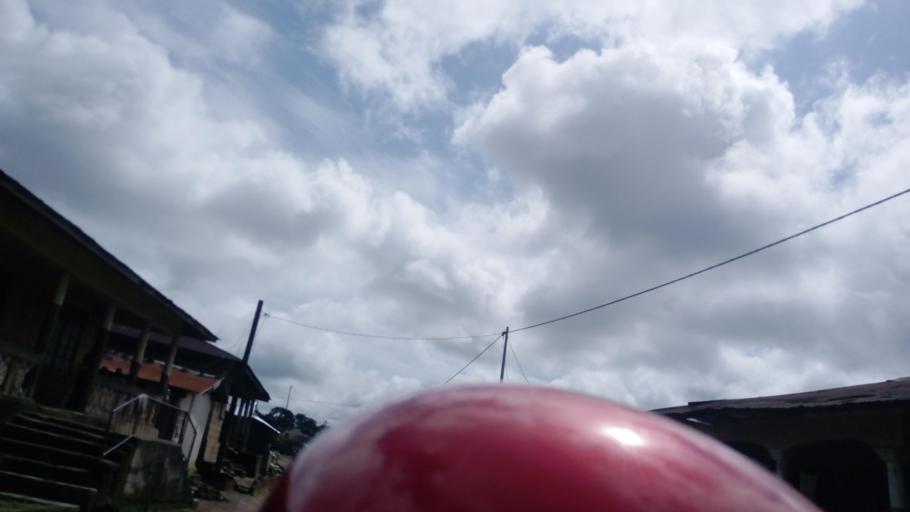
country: SL
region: Northern Province
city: Makeni
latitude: 8.8885
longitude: -12.0396
